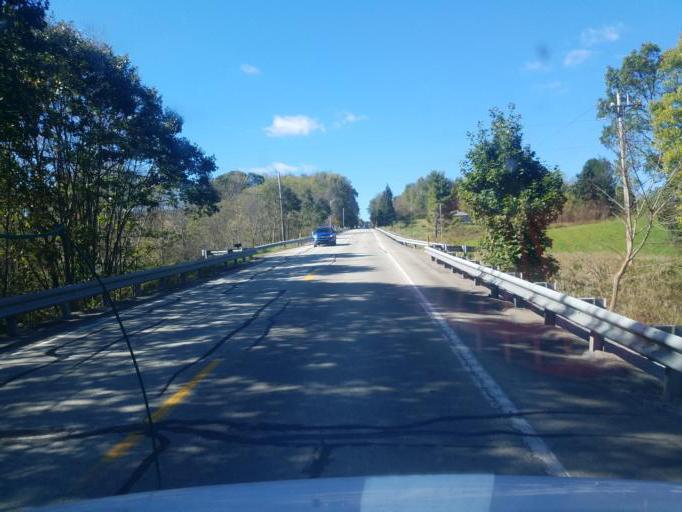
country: US
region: Pennsylvania
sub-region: Somerset County
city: Boswell
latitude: 40.1672
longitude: -79.0960
